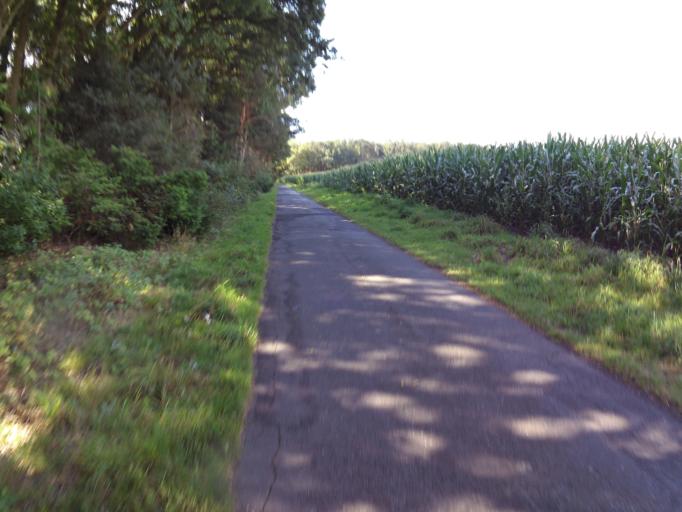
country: DE
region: Lower Saxony
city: Sandbostel
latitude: 53.3979
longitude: 9.1229
